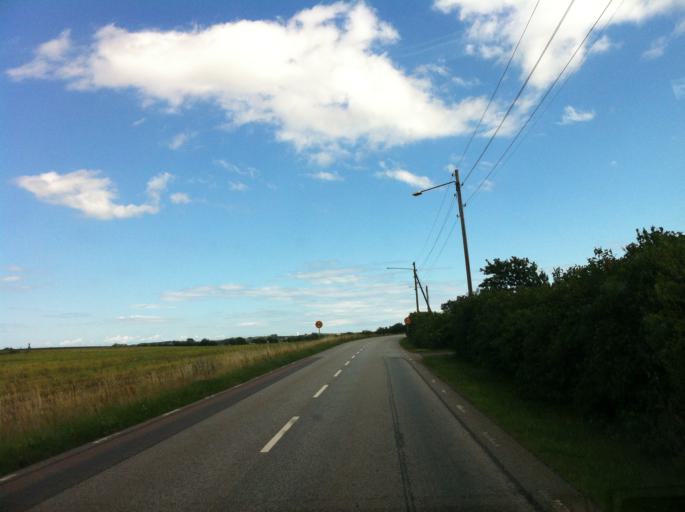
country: SE
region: Skane
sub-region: Ystads Kommun
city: Kopingebro
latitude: 55.4302
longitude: 13.9772
